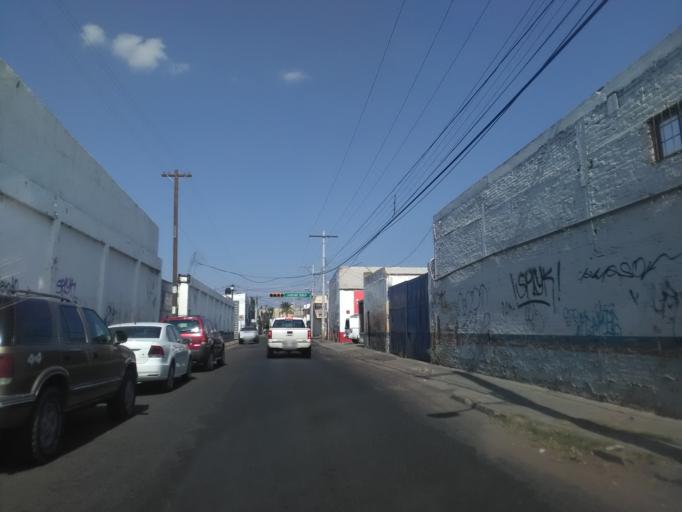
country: MX
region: Durango
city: Victoria de Durango
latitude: 24.0291
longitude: -104.6578
